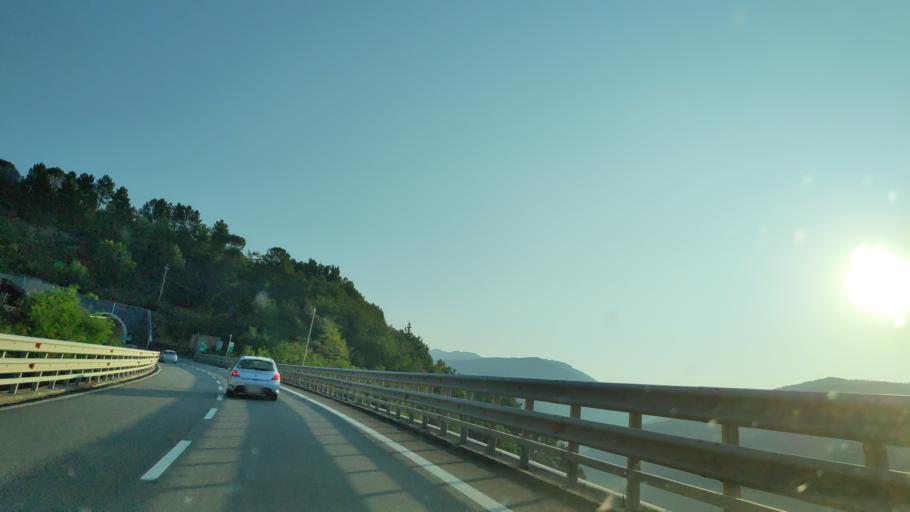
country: IT
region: Calabria
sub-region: Provincia di Cosenza
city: Carpanzano
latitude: 39.1537
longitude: 16.2873
